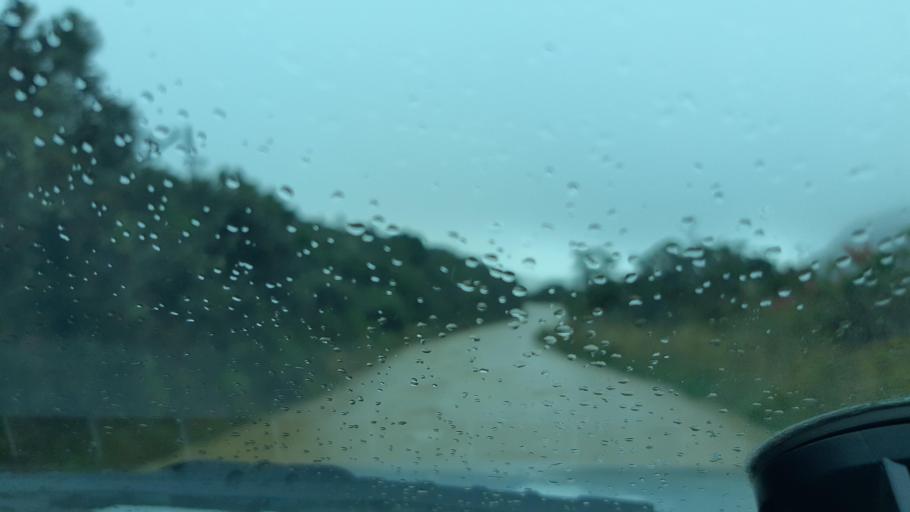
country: CO
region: Cundinamarca
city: Villapinzon
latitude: 5.2176
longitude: -73.5270
